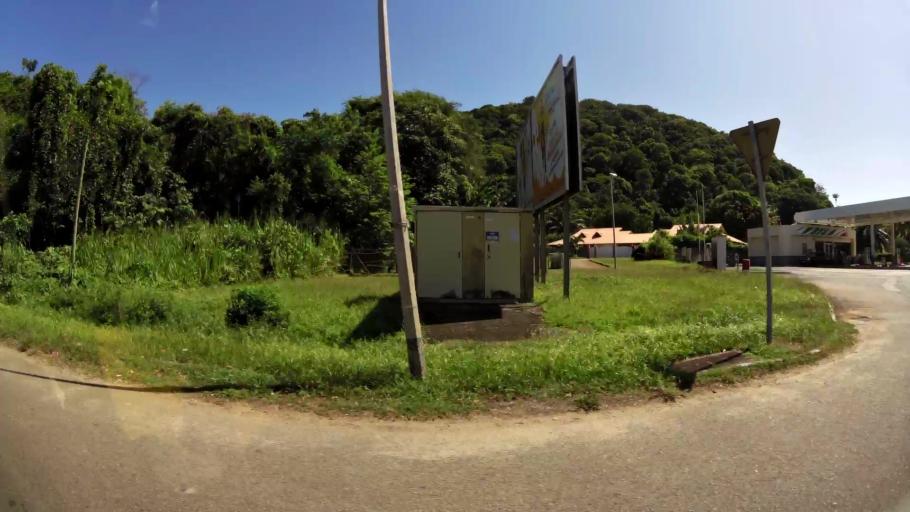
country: GF
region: Guyane
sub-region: Guyane
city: Remire-Montjoly
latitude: 4.9225
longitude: -52.2816
